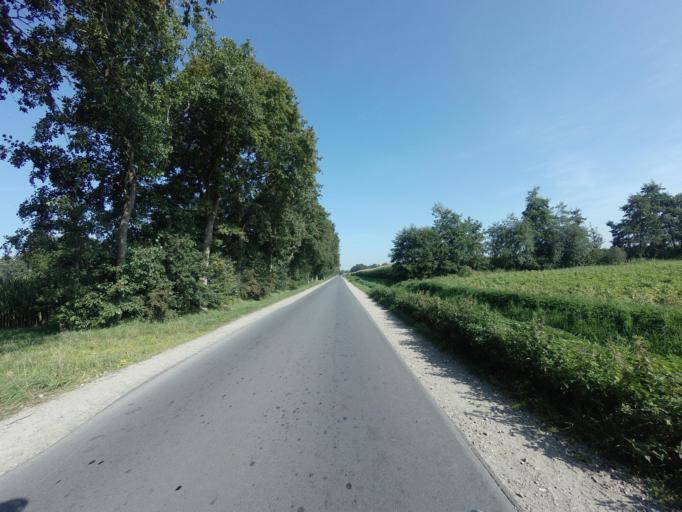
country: DE
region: Lower Saxony
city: Laar
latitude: 52.5843
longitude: 6.7797
